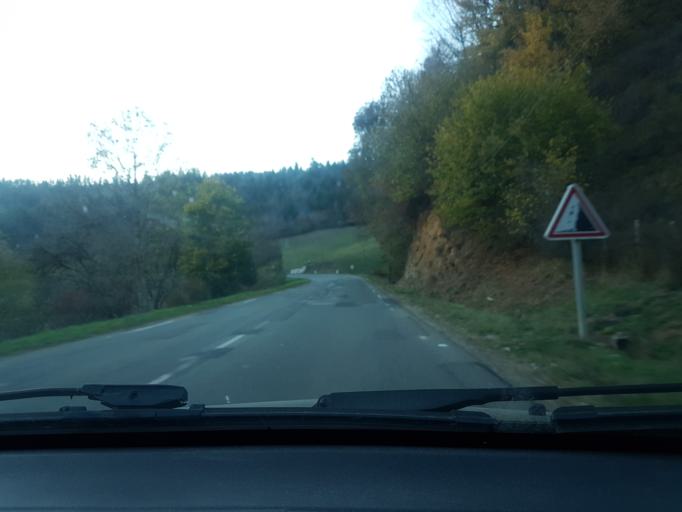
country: FR
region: Franche-Comte
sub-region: Departement du Doubs
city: Villers-le-Lac
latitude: 47.0536
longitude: 6.6608
